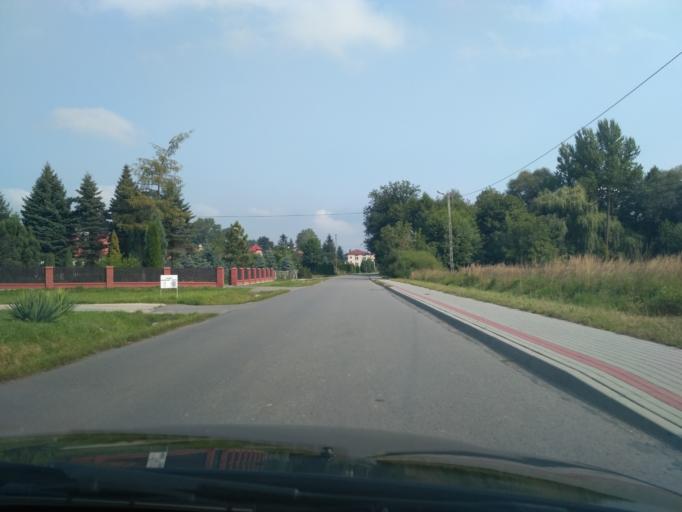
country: PL
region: Subcarpathian Voivodeship
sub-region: Powiat rzeszowski
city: Niechobrz
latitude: 49.9877
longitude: 21.8752
